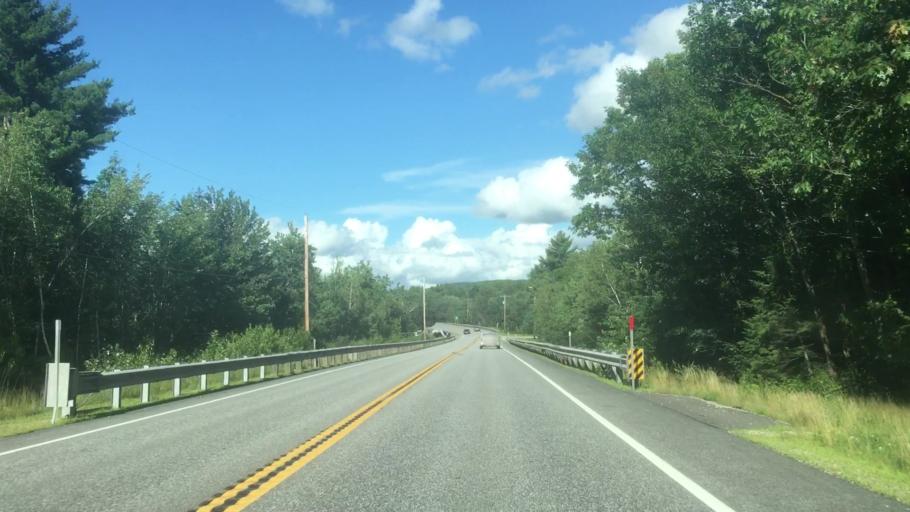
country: US
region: New Hampshire
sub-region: Cheshire County
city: Harrisville
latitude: 43.0378
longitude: -72.0782
